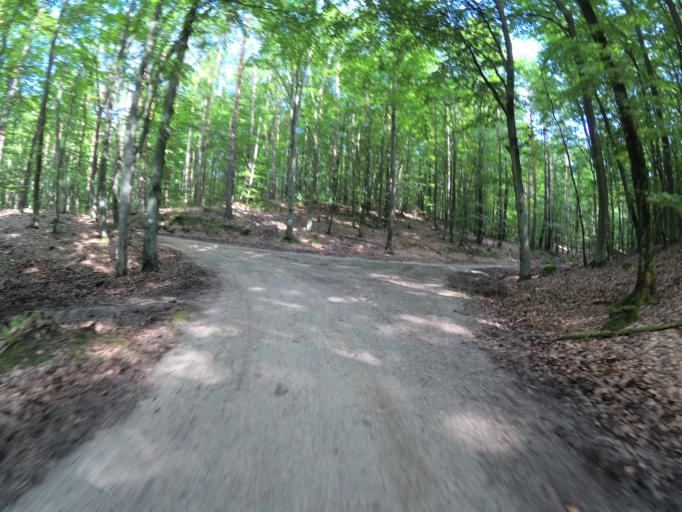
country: PL
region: Pomeranian Voivodeship
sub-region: Gdynia
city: Wielki Kack
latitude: 54.4956
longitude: 18.4798
